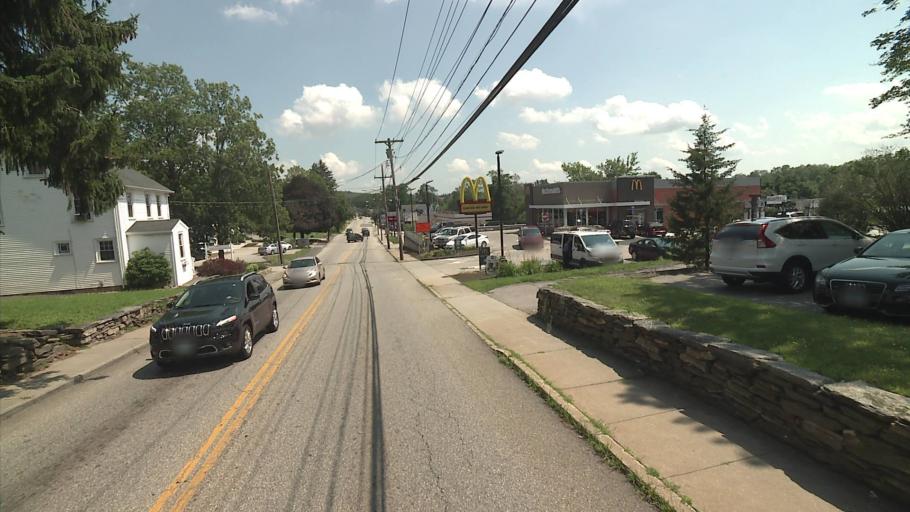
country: US
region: Connecticut
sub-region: New London County
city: Norwich
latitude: 41.5485
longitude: -72.0945
